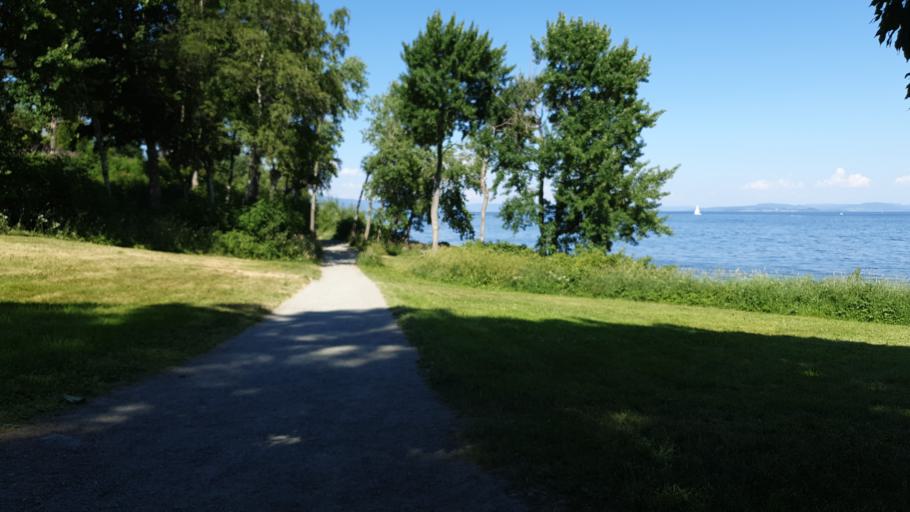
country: NO
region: Sor-Trondelag
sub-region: Trondheim
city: Trondheim
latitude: 63.4500
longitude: 10.4658
